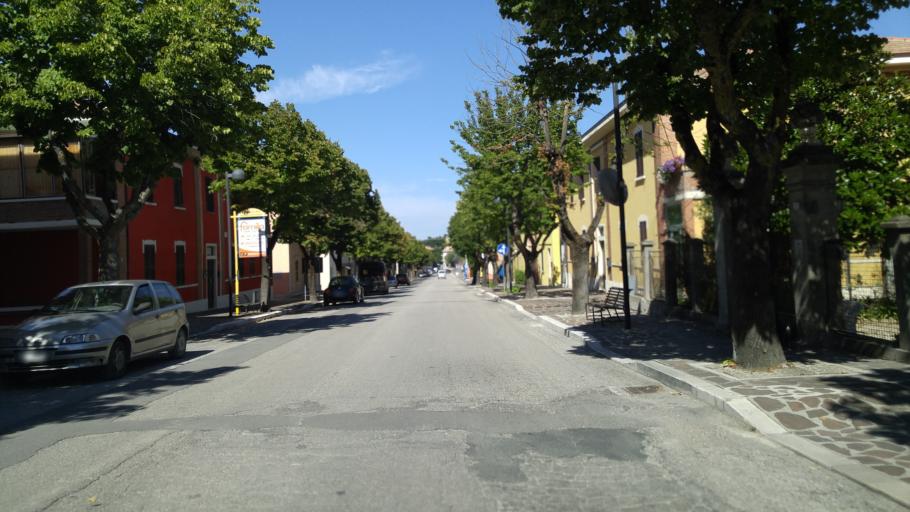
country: IT
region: The Marches
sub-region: Provincia di Pesaro e Urbino
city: Mondavio
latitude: 43.6840
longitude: 12.9597
